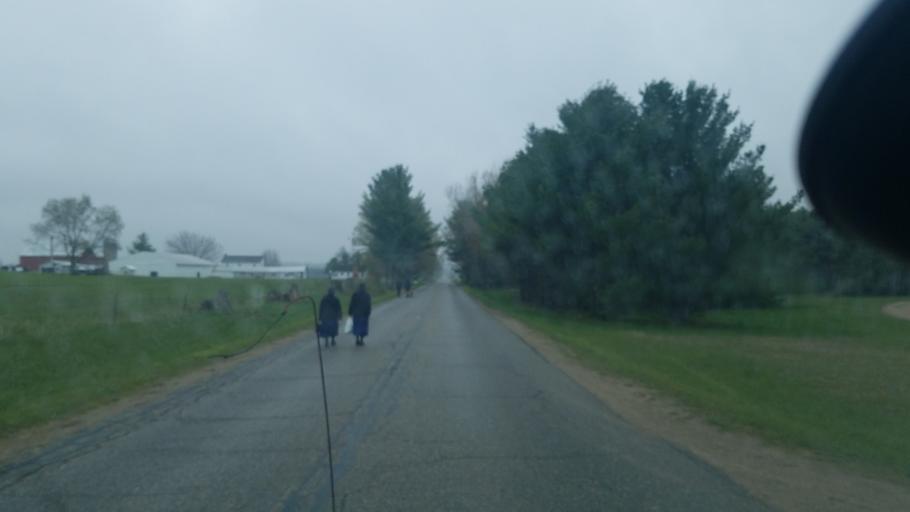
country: US
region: Michigan
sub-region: Montcalm County
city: Lakeview
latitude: 43.5009
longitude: -85.2842
